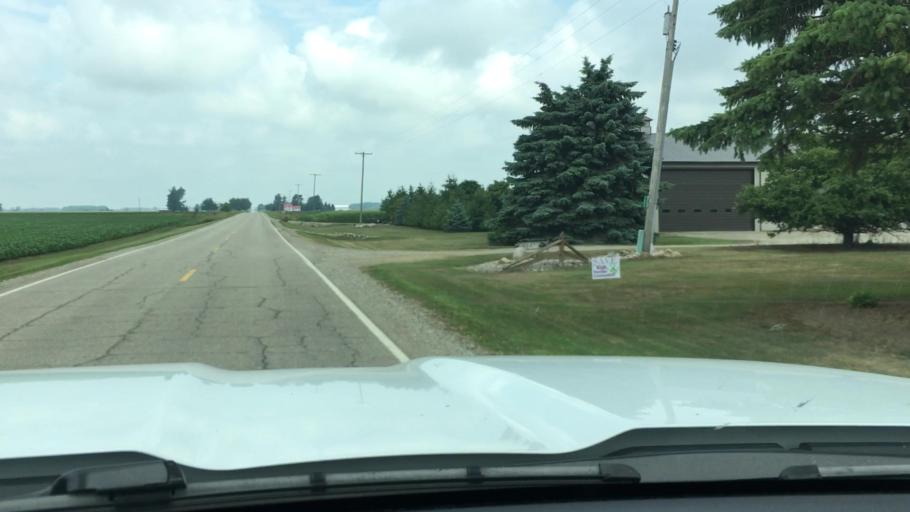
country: US
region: Michigan
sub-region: Sanilac County
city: Marlette
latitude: 43.3674
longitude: -83.0060
